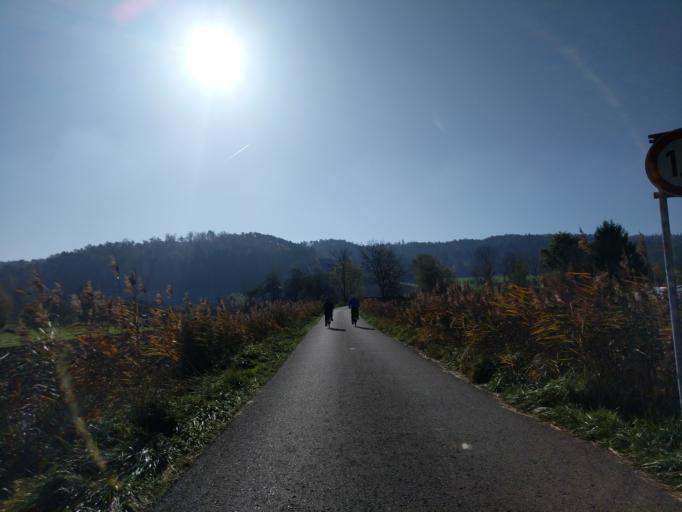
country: DE
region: Baden-Wuerttemberg
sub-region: Tuebingen Region
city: Tuebingen
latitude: 48.5216
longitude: 9.0238
